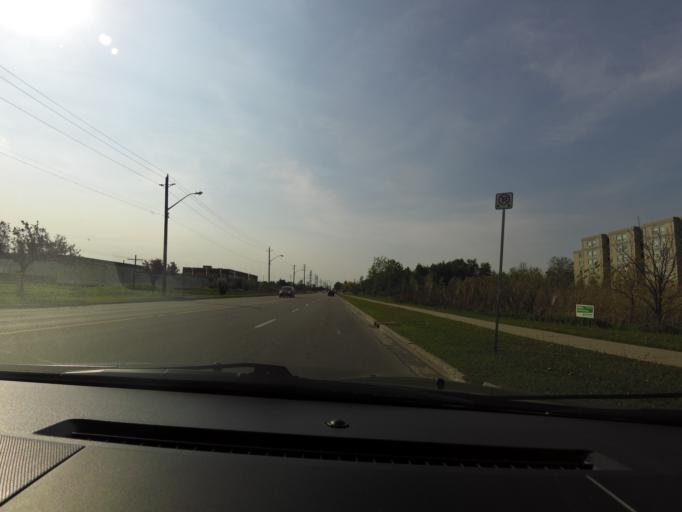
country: CA
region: Ontario
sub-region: Wellington County
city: Guelph
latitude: 43.5493
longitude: -80.2744
